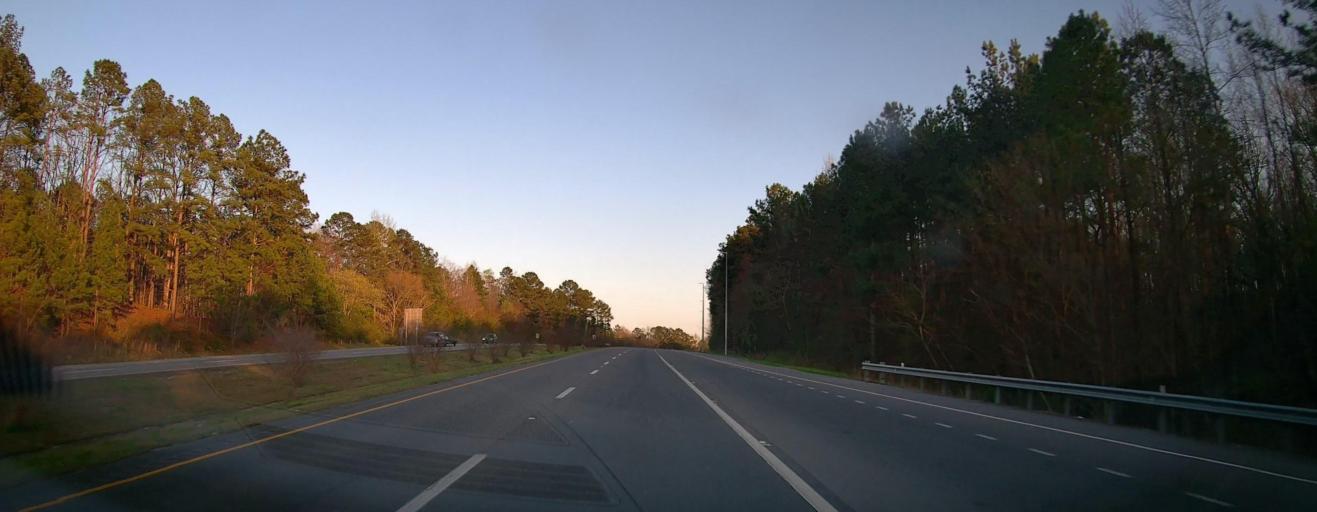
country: US
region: Alabama
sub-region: Talladega County
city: Sylacauga
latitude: 33.1420
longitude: -86.2539
